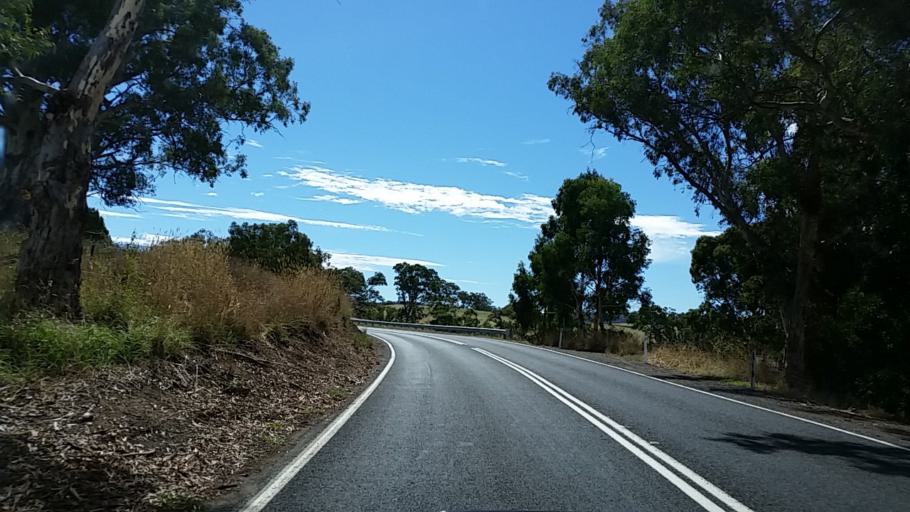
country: AU
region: South Australia
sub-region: Adelaide Hills
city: Gumeracha
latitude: -34.8218
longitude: 138.9130
